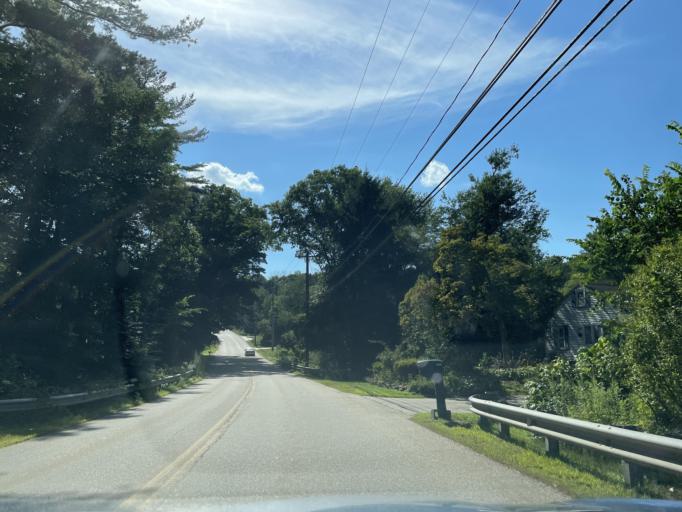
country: US
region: Massachusetts
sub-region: Worcester County
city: Oxford
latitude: 42.1199
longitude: -71.8947
